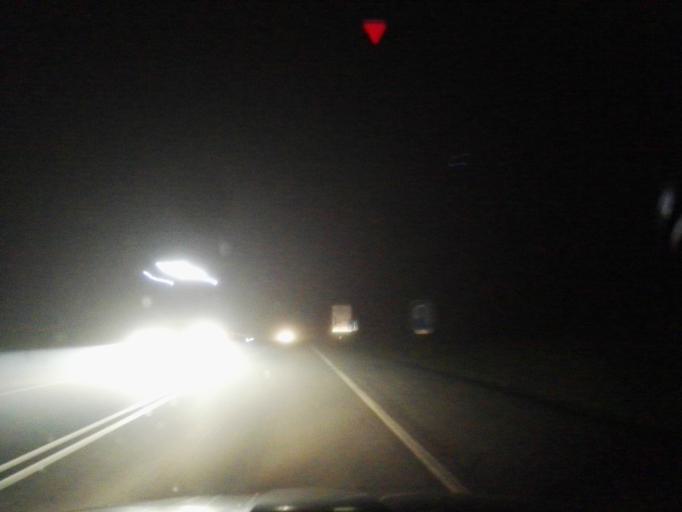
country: PT
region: Evora
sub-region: Vila Vicosa
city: Vila Vicosa
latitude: 38.8473
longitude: -7.3629
